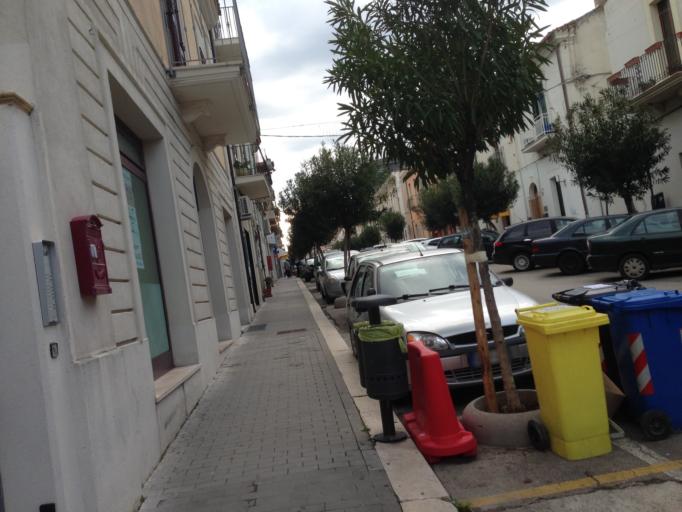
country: IT
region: Molise
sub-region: Provincia di Campobasso
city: Termoli
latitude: 42.0031
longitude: 14.9967
